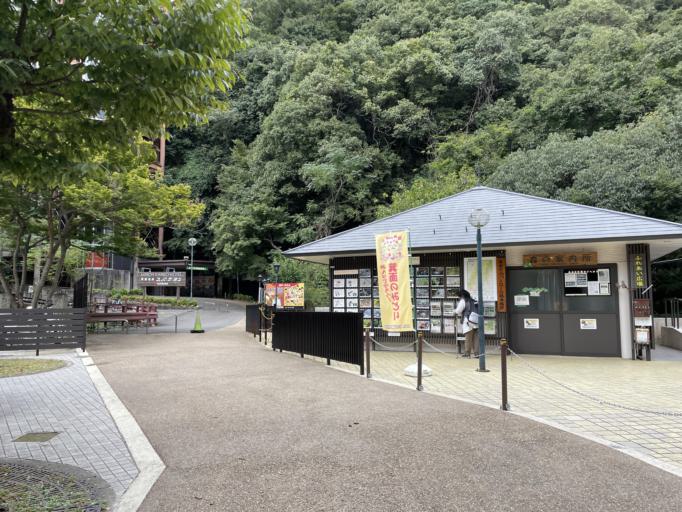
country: JP
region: Osaka
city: Mino
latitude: 34.8374
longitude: 135.4685
